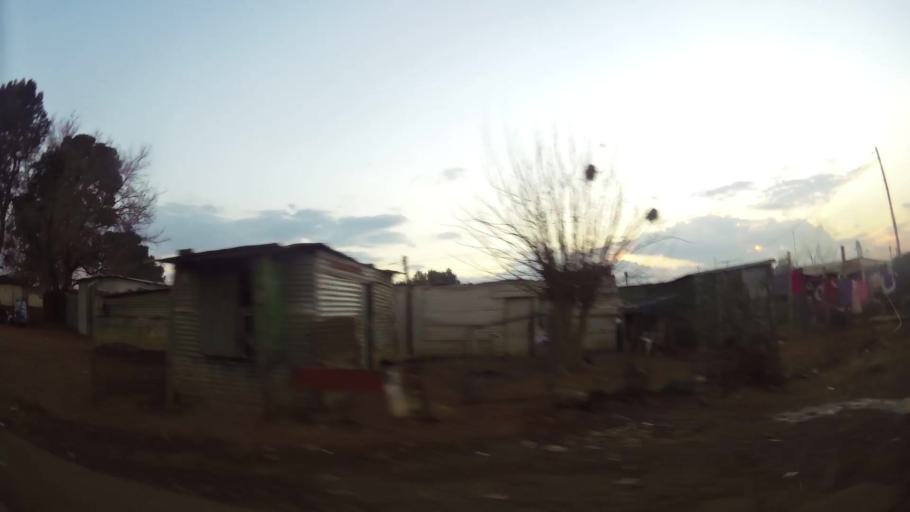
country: ZA
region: Gauteng
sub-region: City of Johannesburg Metropolitan Municipality
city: Orange Farm
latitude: -26.5562
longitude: 27.8611
